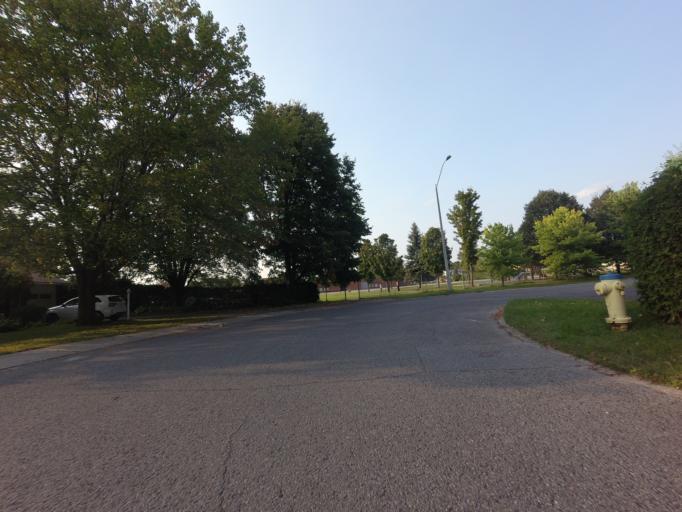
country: CA
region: Ontario
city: Bells Corners
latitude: 45.2825
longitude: -75.7602
